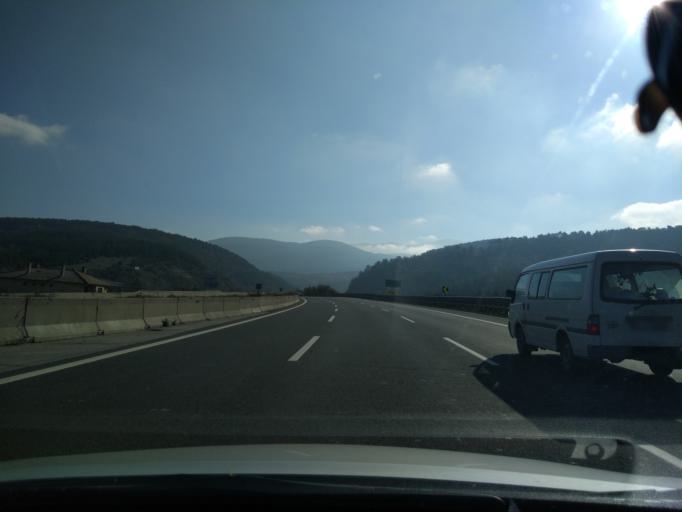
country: TR
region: Bolu
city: Bolu
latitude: 40.7536
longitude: 31.7747
